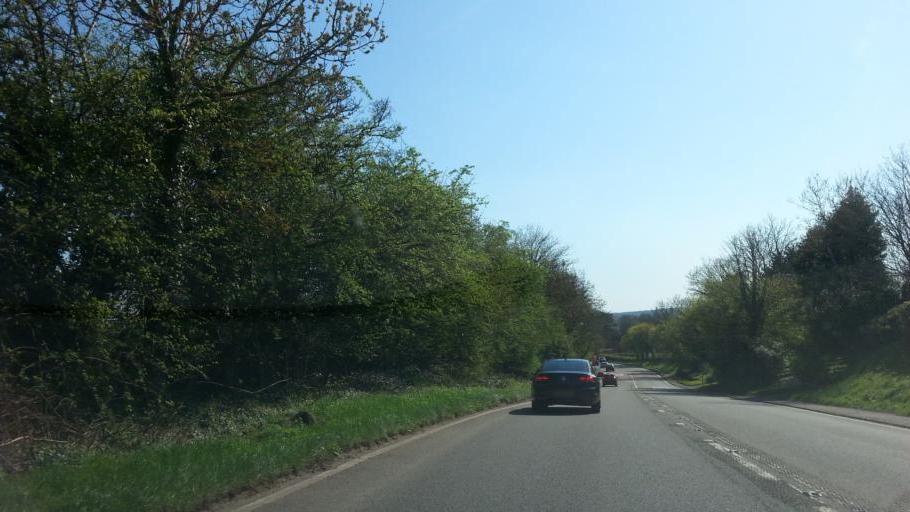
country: GB
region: England
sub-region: Worcestershire
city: Alvechurch
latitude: 52.3807
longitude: -1.9580
